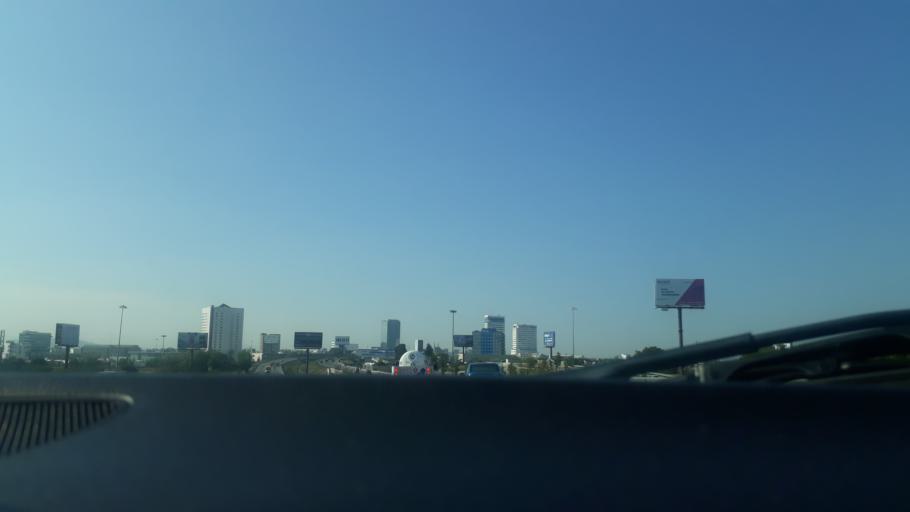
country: MX
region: Puebla
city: Tlazcalancingo
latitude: 19.0080
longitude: -98.2605
